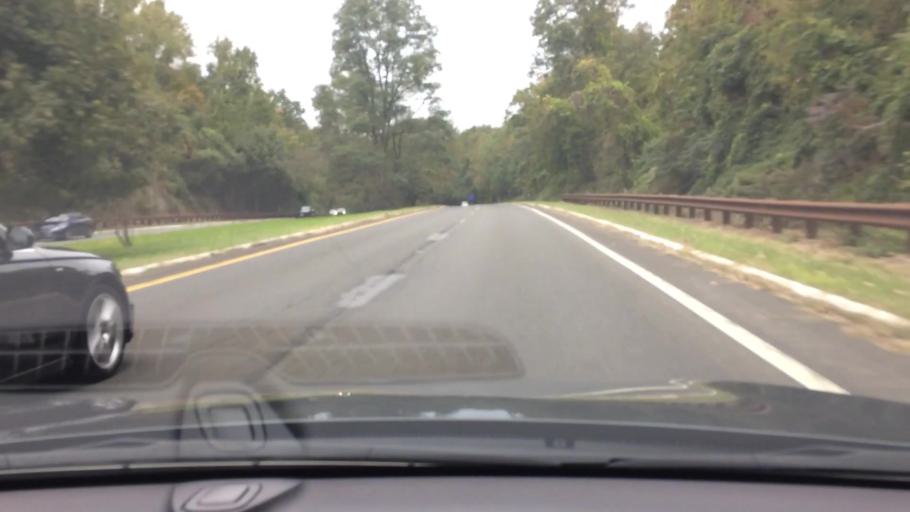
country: US
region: New York
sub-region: Rockland County
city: Sparkill
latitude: 41.0134
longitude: -73.9245
